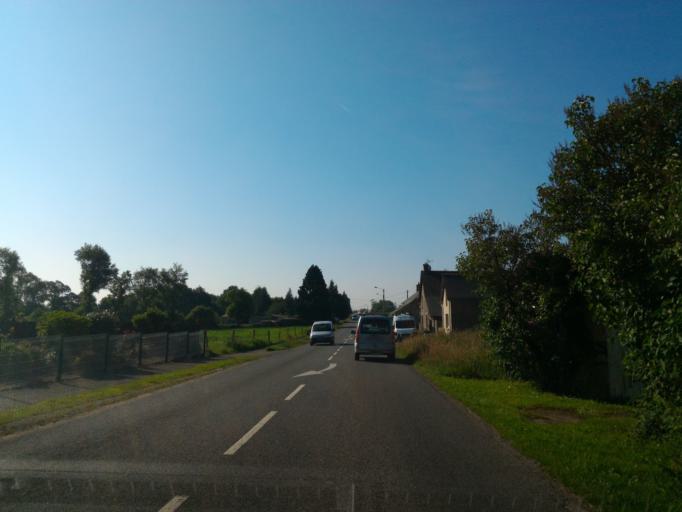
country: FR
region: Pays de la Loire
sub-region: Departement de la Mayenne
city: Juvigne
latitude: 48.2217
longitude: -1.0938
